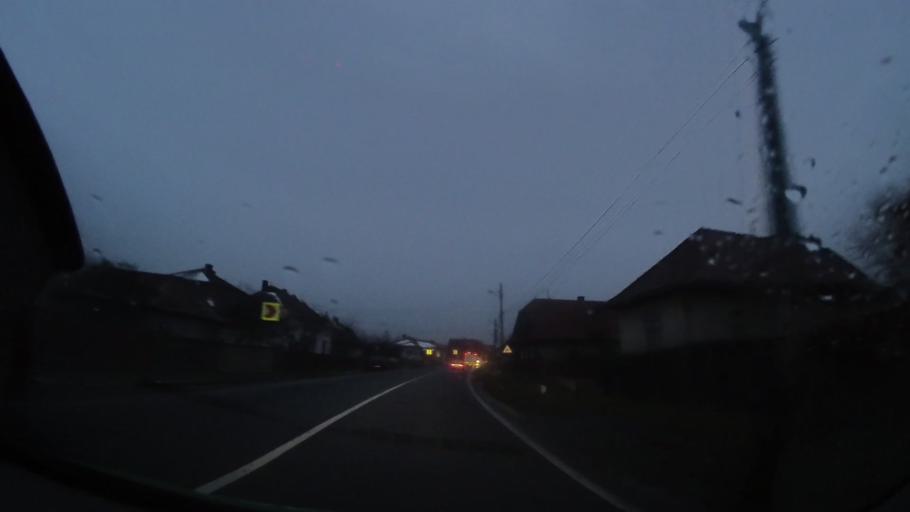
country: RO
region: Harghita
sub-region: Comuna Ditrau
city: Ditrau
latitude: 46.8084
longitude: 25.4930
